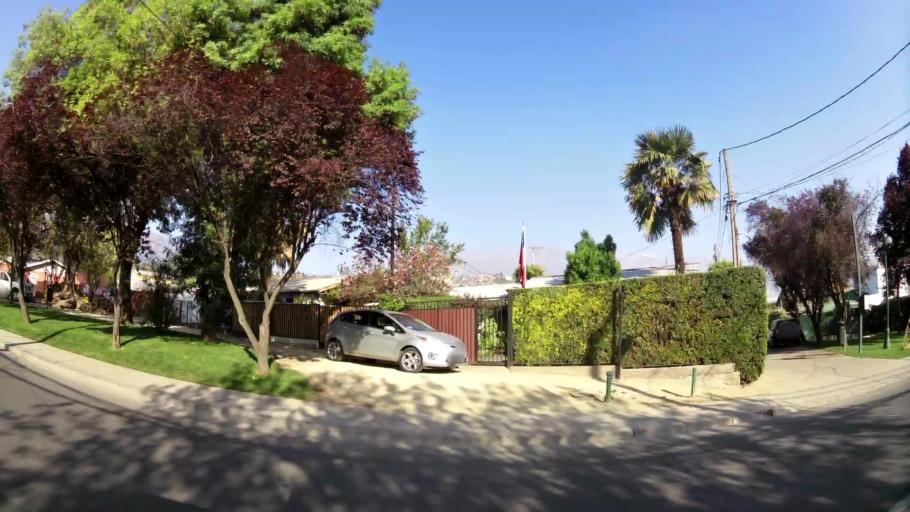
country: CL
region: Santiago Metropolitan
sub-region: Provincia de Santiago
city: Villa Presidente Frei, Nunoa, Santiago, Chile
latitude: -33.3530
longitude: -70.5071
